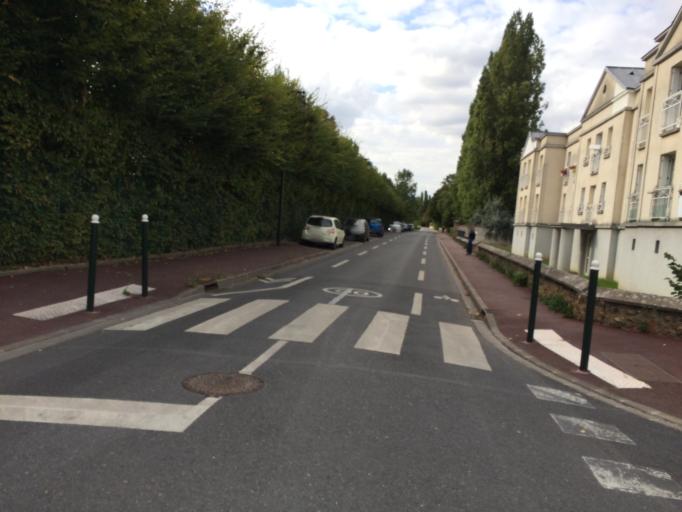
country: FR
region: Ile-de-France
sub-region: Departement de l'Essonne
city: Soisy-sur-Seine
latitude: 48.6492
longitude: 2.4423
